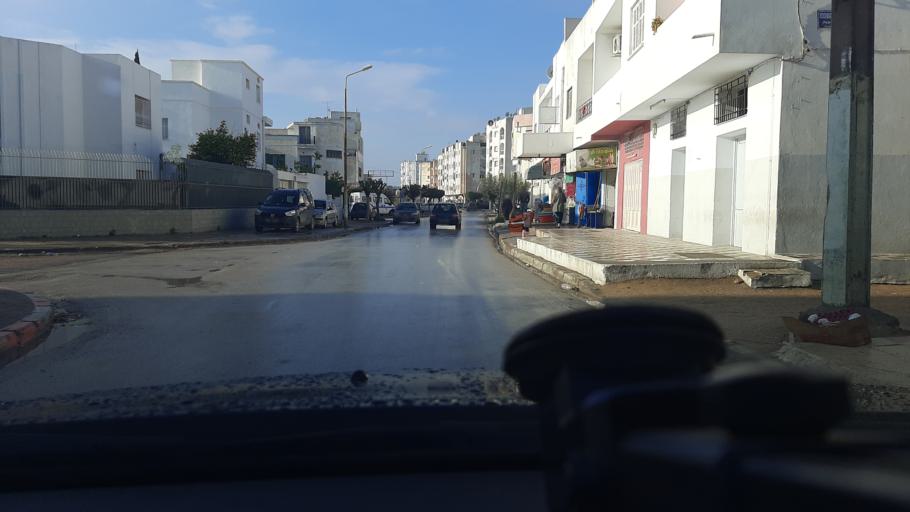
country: TN
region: Safaqis
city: Sfax
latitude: 34.7436
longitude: 10.7509
